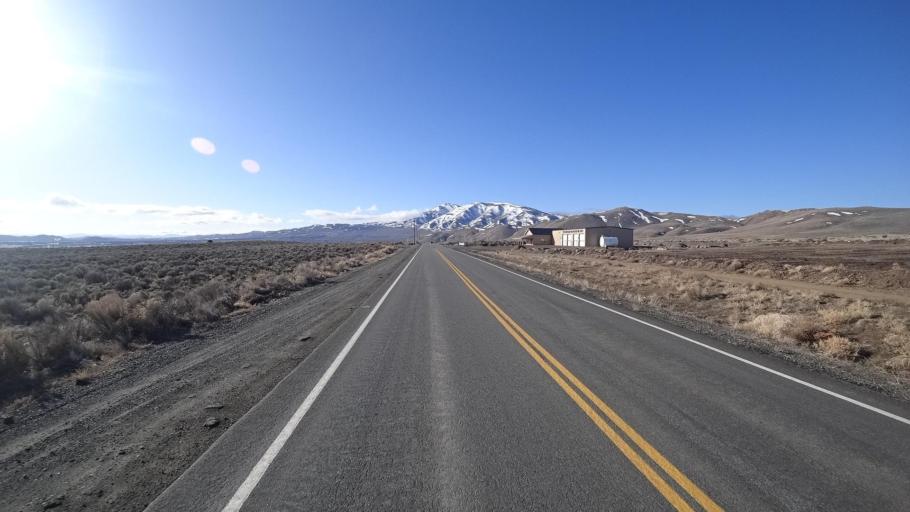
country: US
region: Nevada
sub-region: Washoe County
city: Cold Springs
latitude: 39.6729
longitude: -119.9224
